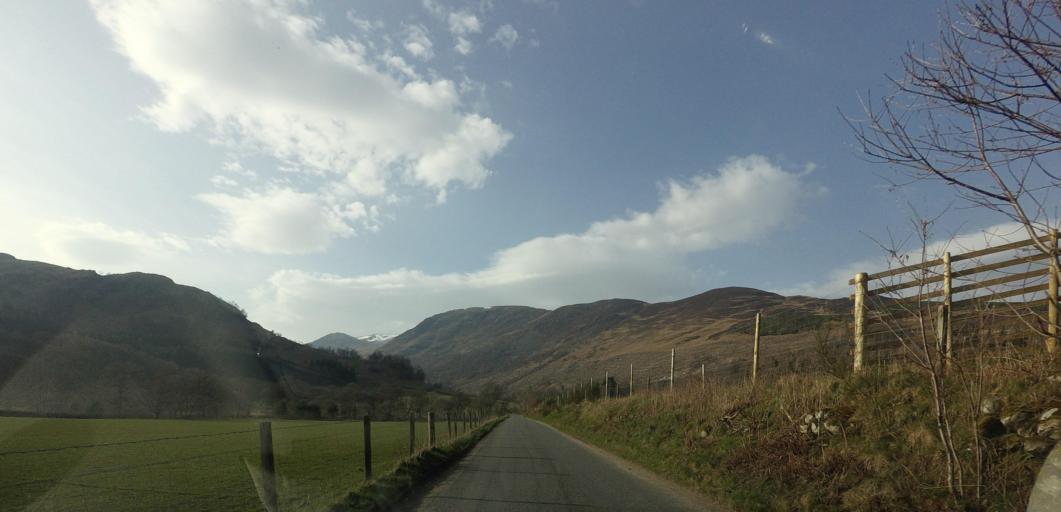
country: GB
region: Scotland
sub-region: Perth and Kinross
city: Aberfeldy
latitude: 56.5975
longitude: -4.0689
